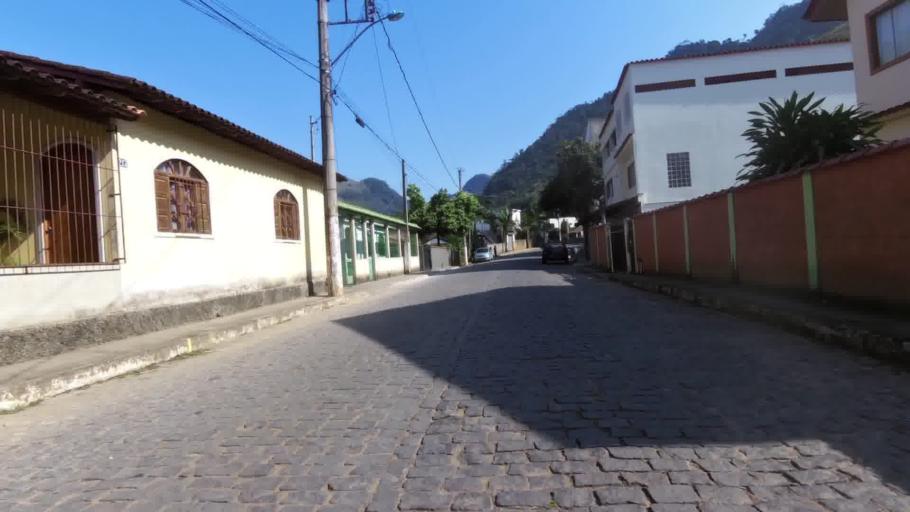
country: BR
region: Espirito Santo
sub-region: Alfredo Chaves
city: Alfredo Chaves
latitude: -20.6293
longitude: -40.7645
